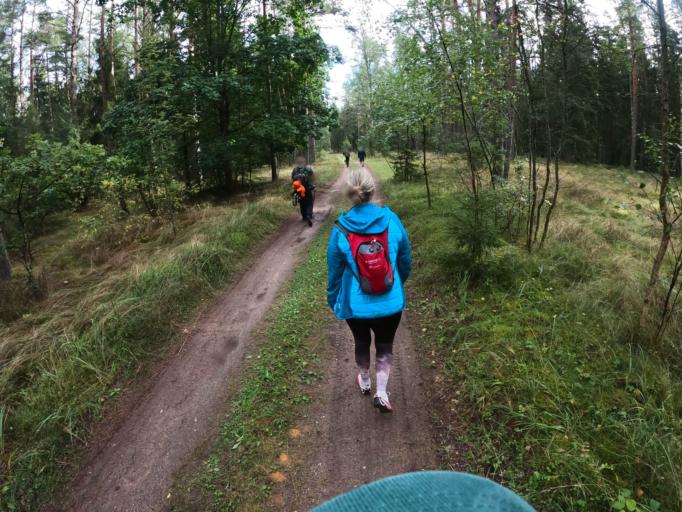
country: LV
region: Engure
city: Smarde
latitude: 56.9833
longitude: 23.3389
